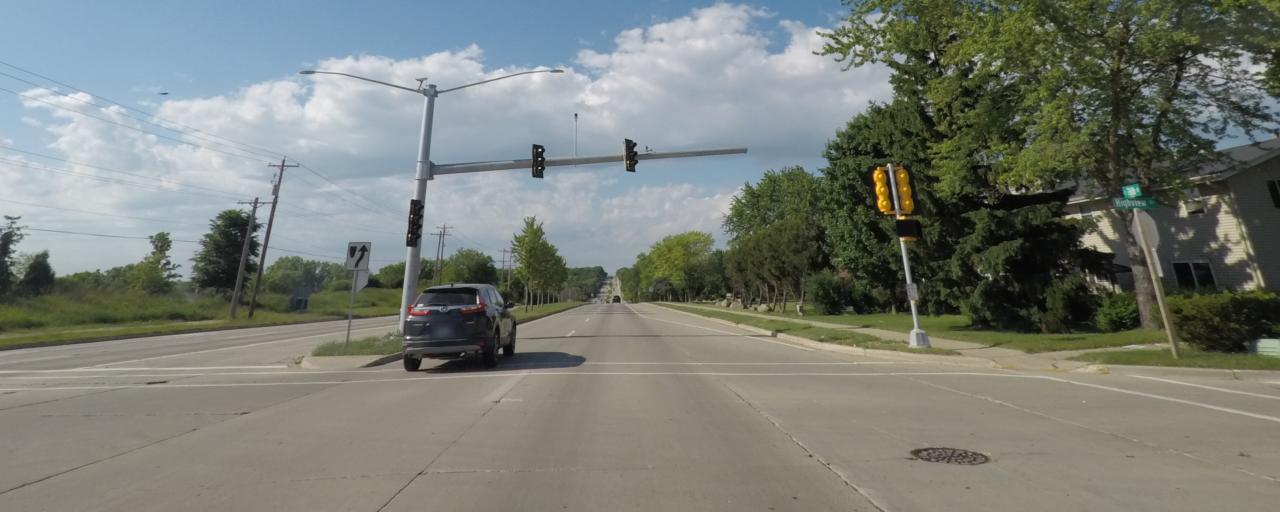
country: US
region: Wisconsin
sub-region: Milwaukee County
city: Greendale
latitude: 42.9223
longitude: -88.0089
